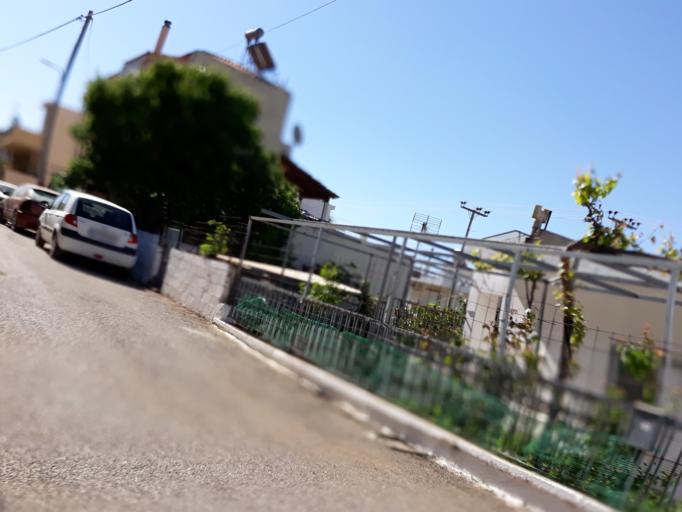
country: GR
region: Attica
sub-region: Nomarchia Dytikis Attikis
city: Ano Liosia
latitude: 38.0945
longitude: 23.7104
